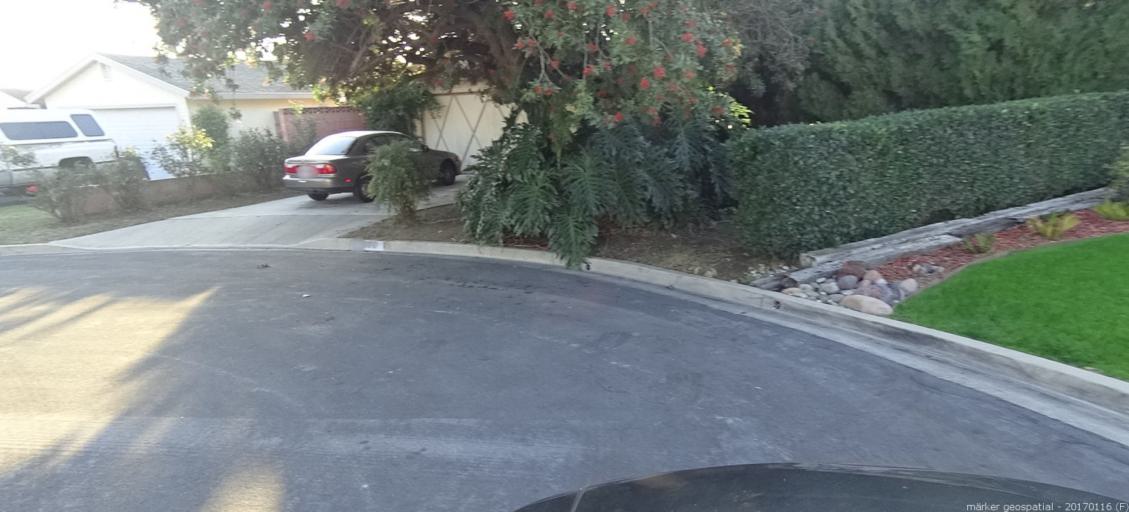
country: US
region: California
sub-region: Orange County
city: Stanton
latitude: 33.8047
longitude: -117.9782
